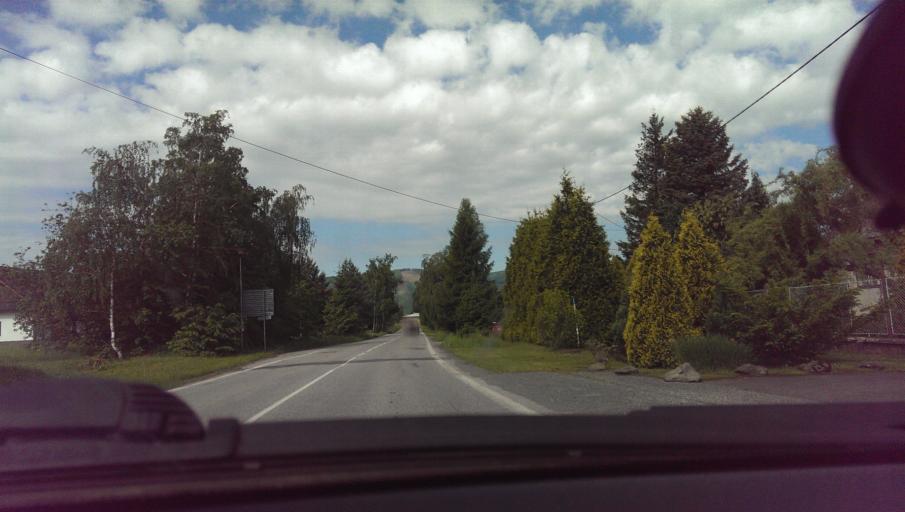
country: CZ
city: Trojanovice
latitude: 49.5232
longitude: 18.2361
